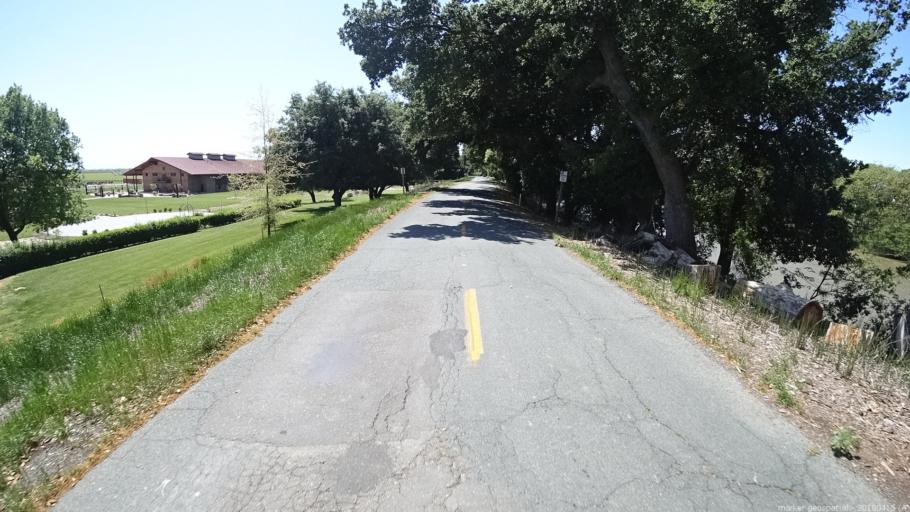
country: US
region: California
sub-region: Sacramento County
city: Walnut Grove
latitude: 38.3033
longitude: -121.5766
